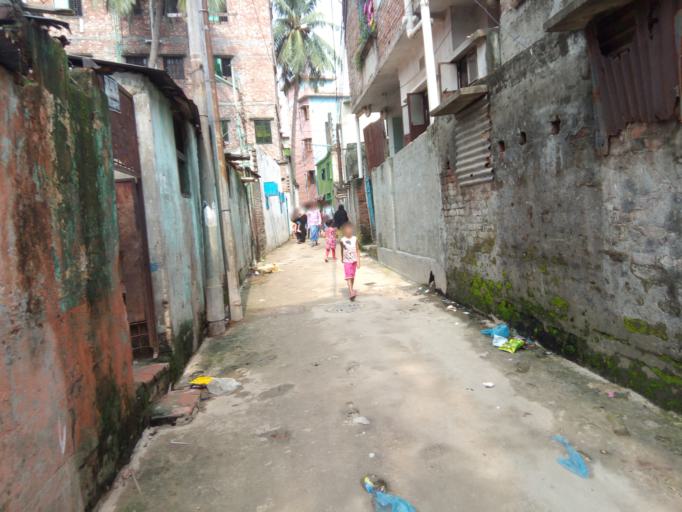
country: BD
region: Dhaka
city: Azimpur
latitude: 23.7377
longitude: 90.3636
